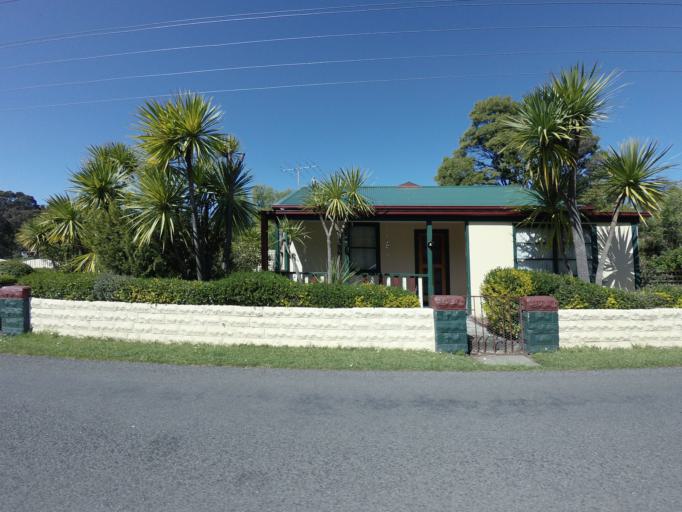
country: AU
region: Tasmania
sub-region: Derwent Valley
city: New Norfolk
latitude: -42.6798
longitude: 146.7857
